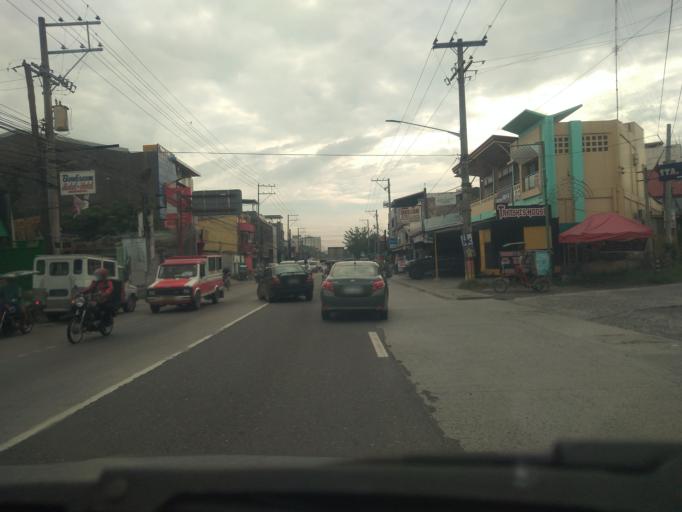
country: PH
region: Central Luzon
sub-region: Province of Pampanga
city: San Fernando
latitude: 15.0334
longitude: 120.6886
